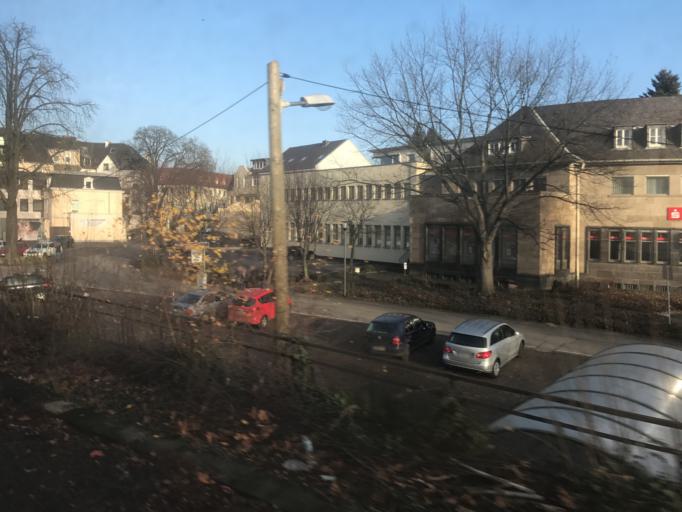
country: DE
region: North Rhine-Westphalia
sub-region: Regierungsbezirk Koln
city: Konigswinter
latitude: 50.6852
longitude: 7.1576
